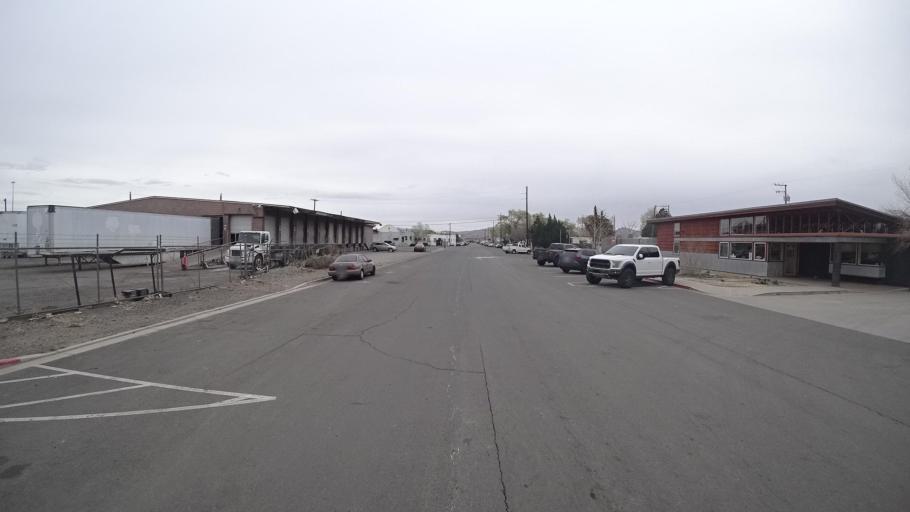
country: US
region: Nevada
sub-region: Washoe County
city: Reno
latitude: 39.5353
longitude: -119.7862
